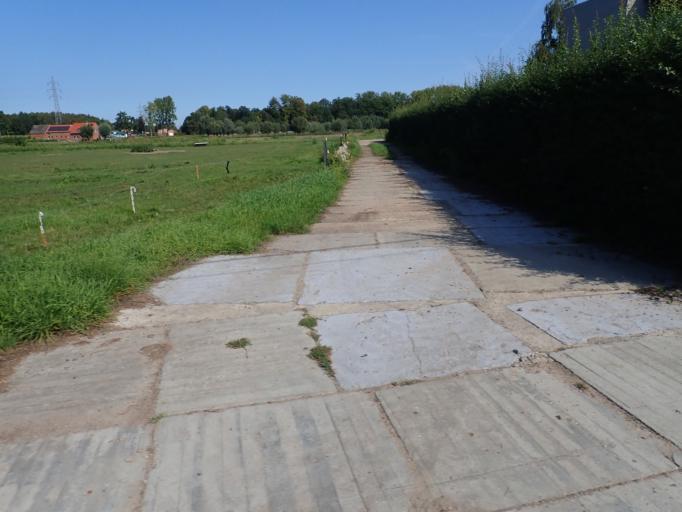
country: BE
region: Flanders
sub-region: Provincie Antwerpen
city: Puurs
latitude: 51.0403
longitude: 4.2767
